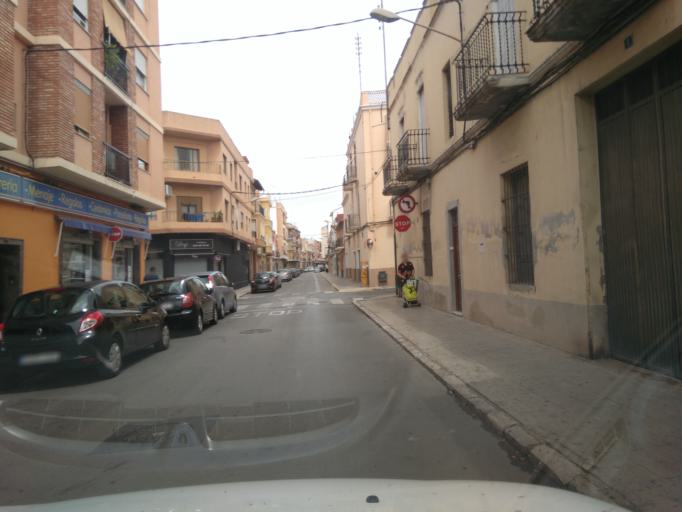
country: ES
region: Valencia
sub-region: Provincia de Valencia
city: Carcaixent
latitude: 39.1230
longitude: -0.4471
